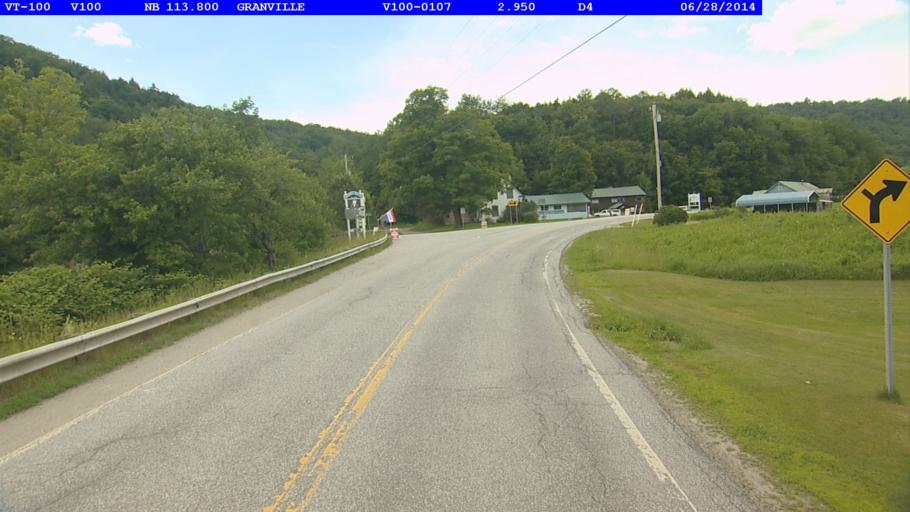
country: US
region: Vermont
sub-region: Orange County
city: Randolph
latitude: 43.9851
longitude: -72.8475
